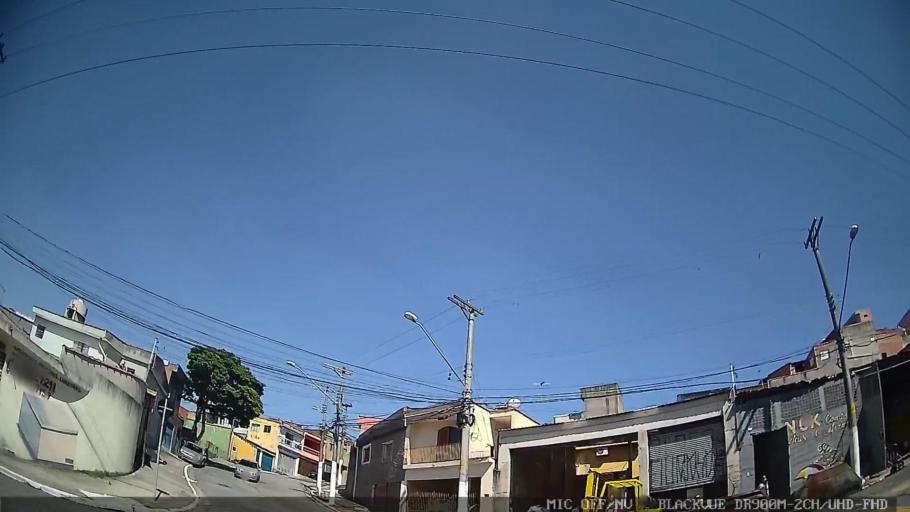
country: BR
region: Sao Paulo
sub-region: Sao Caetano Do Sul
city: Sao Caetano do Sul
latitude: -23.5991
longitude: -46.4944
